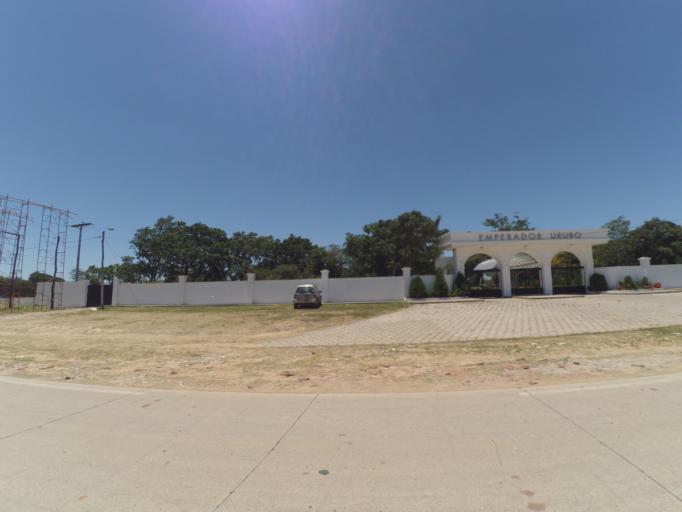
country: BO
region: Santa Cruz
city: Santa Cruz de la Sierra
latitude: -17.7649
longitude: -63.2379
